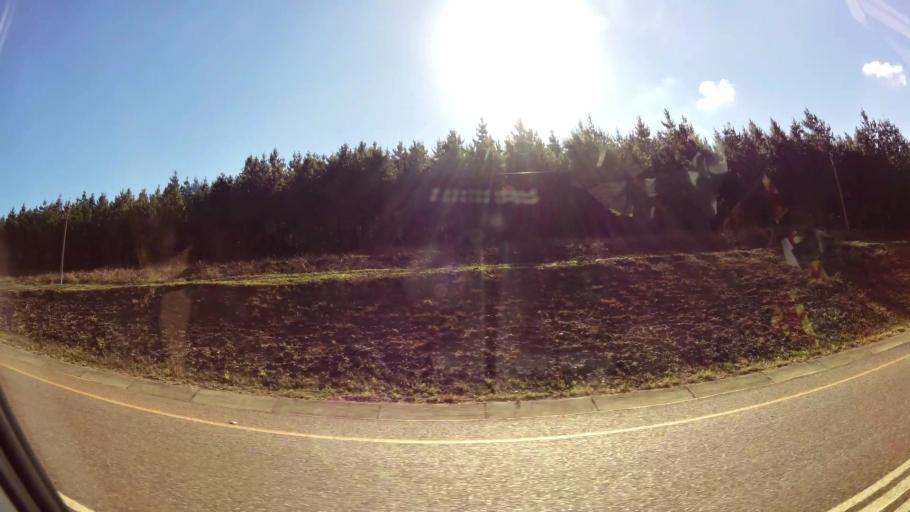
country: ZA
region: Limpopo
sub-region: Capricorn District Municipality
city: Mankoeng
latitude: -23.9130
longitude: 29.9640
